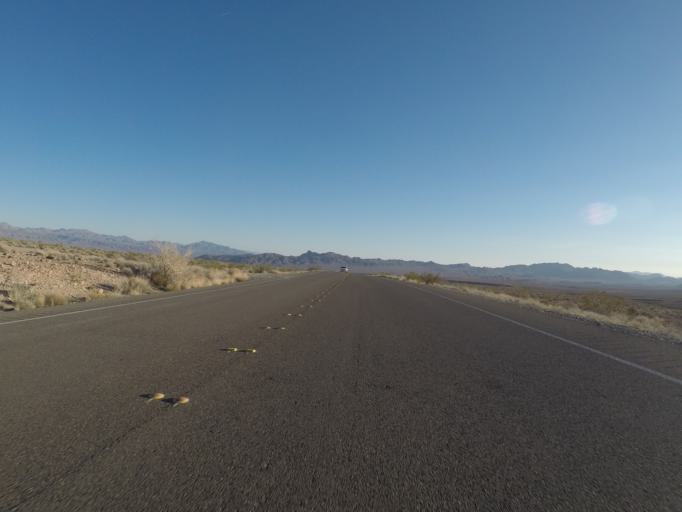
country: US
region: Nevada
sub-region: Clark County
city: Moapa Valley
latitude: 36.3577
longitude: -114.4835
